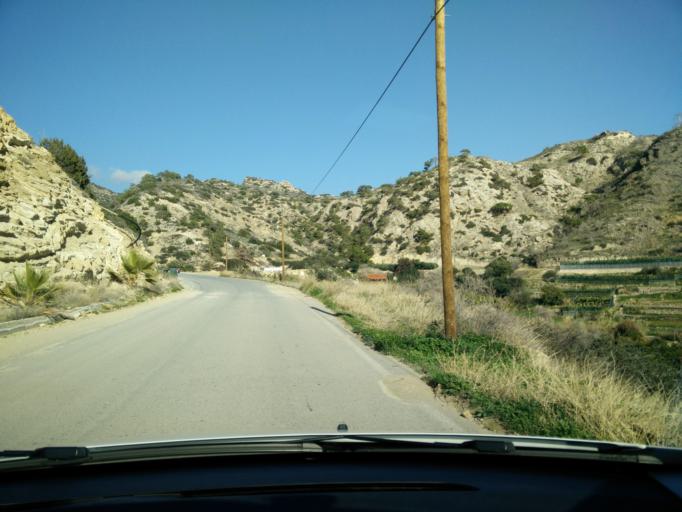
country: GR
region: Crete
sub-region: Nomos Lasithiou
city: Gra Liyia
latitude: 34.9941
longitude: 25.5322
